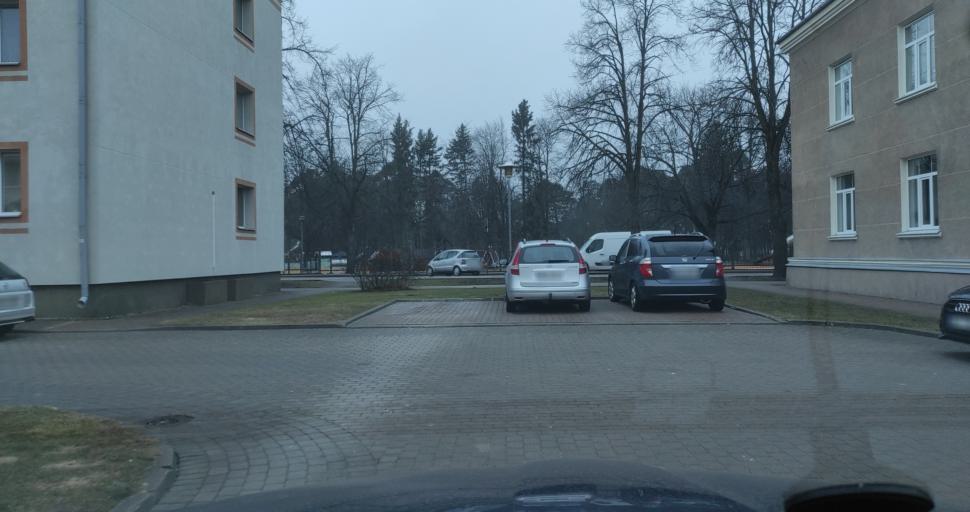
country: LV
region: Ventspils
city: Ventspils
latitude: 57.3886
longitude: 21.5499
